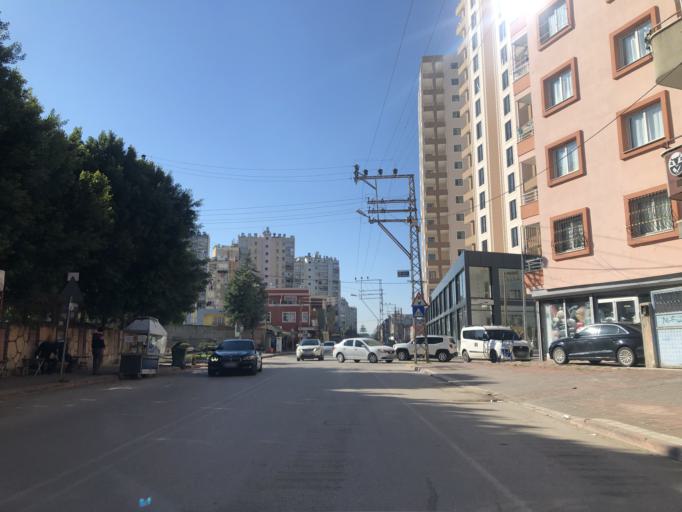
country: TR
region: Adana
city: Yuregir
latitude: 37.0076
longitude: 35.3634
